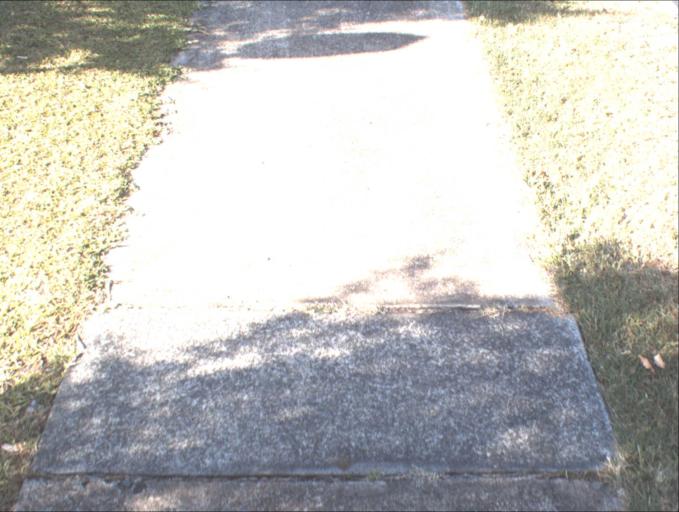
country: AU
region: Queensland
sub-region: Gold Coast
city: Yatala
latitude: -27.7054
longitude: 153.2173
